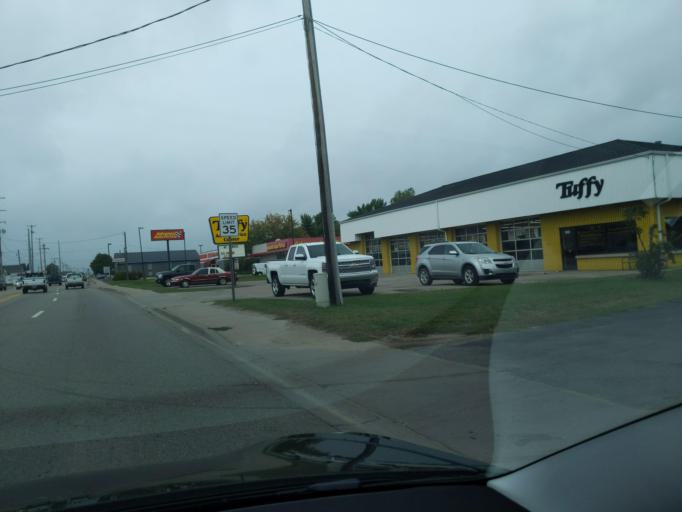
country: US
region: Michigan
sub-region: Wexford County
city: Cadillac
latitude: 44.2616
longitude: -85.4054
